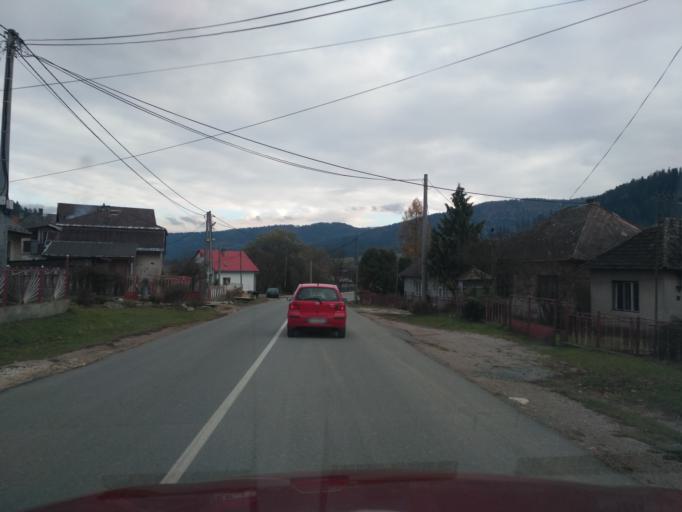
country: SK
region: Kosicky
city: Krompachy
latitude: 48.8095
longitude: 20.7231
